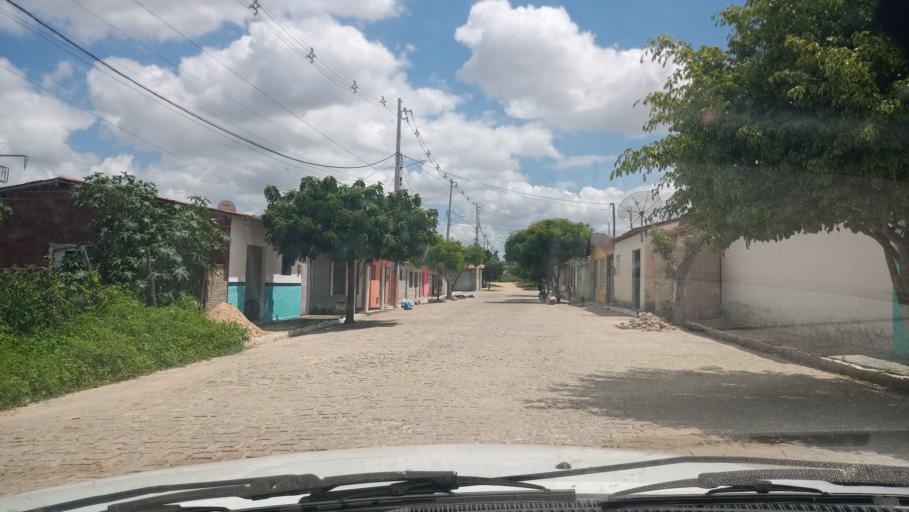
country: BR
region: Rio Grande do Norte
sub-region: Nova Cruz
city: Nova Cruz
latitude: -6.4589
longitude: -35.5792
